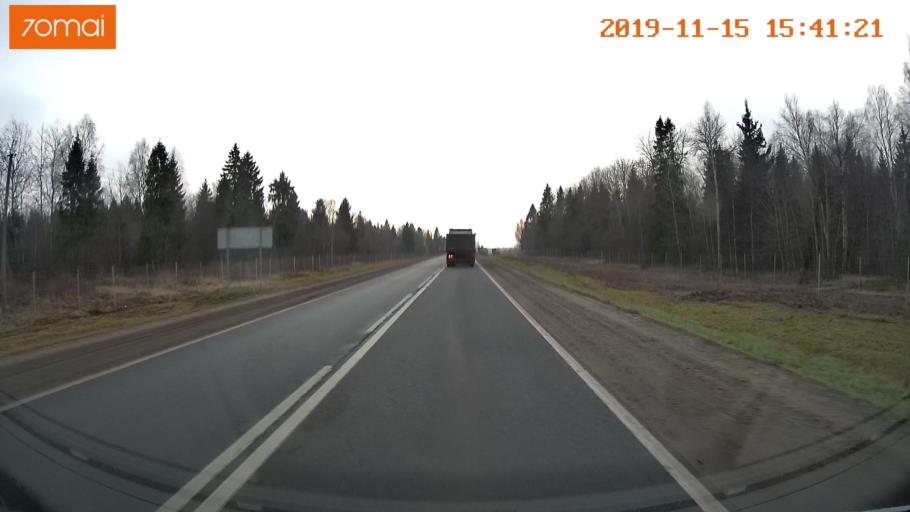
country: RU
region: Jaroslavl
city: Danilov
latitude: 58.0016
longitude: 40.0488
